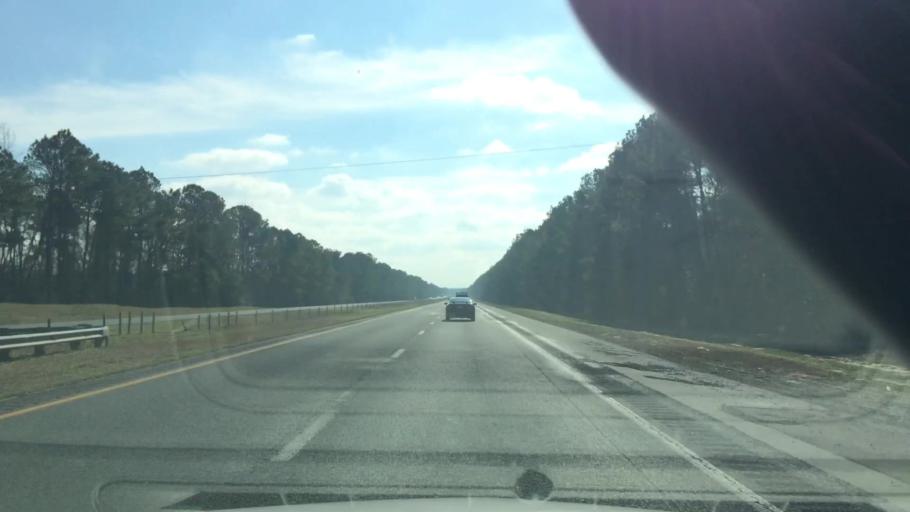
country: US
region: North Carolina
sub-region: Duplin County
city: Wallace
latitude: 34.7319
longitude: -77.9449
